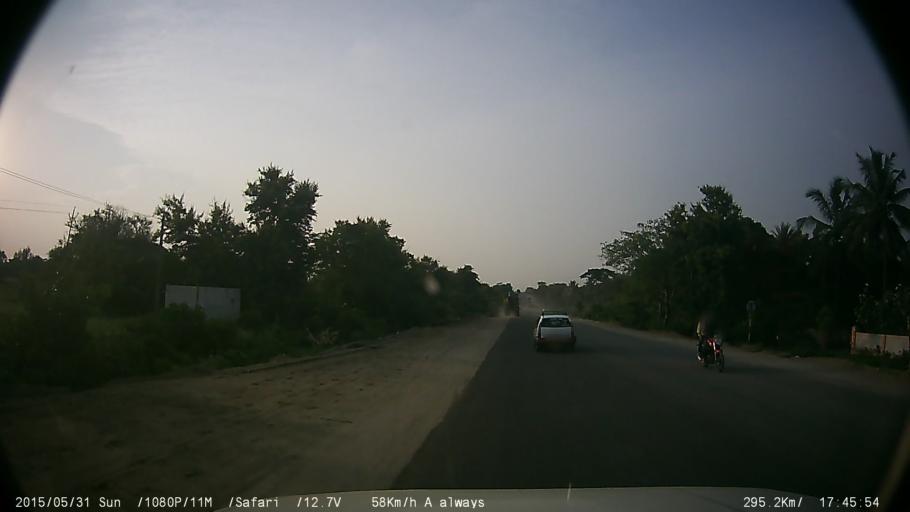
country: IN
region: Karnataka
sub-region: Chamrajnagar
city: Gundlupet
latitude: 11.9548
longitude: 76.6705
